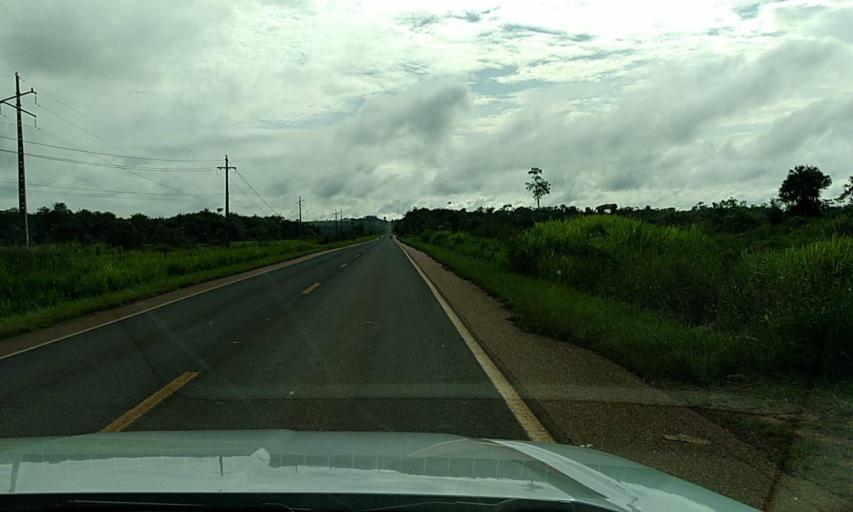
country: BR
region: Para
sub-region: Altamira
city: Altamira
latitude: -3.1725
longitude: -52.1487
